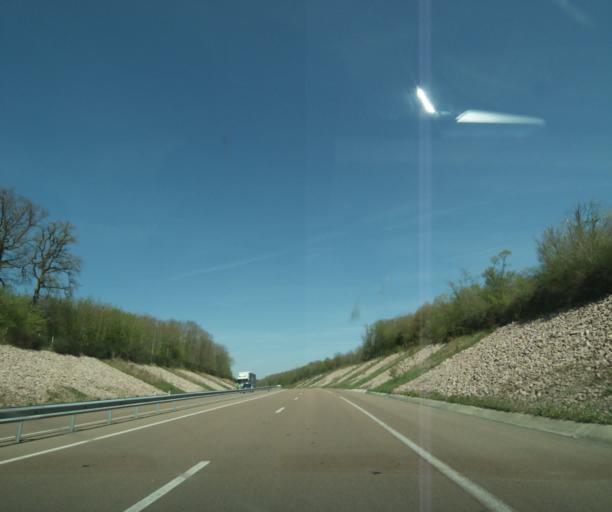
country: FR
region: Bourgogne
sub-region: Departement de la Nievre
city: Challuy
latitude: 46.9194
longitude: 3.1624
